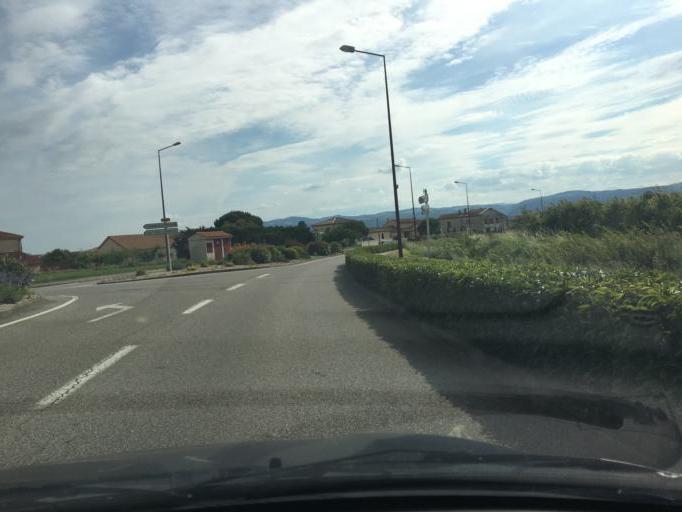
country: FR
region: Rhone-Alpes
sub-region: Departement de la Drome
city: Mercurol
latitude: 45.0746
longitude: 4.8892
